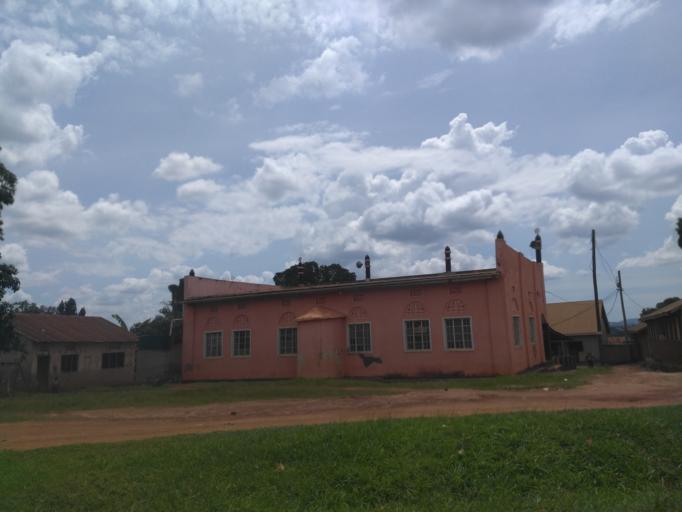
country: UG
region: Central Region
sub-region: Wakiso District
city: Kireka
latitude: 0.4419
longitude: 32.6070
